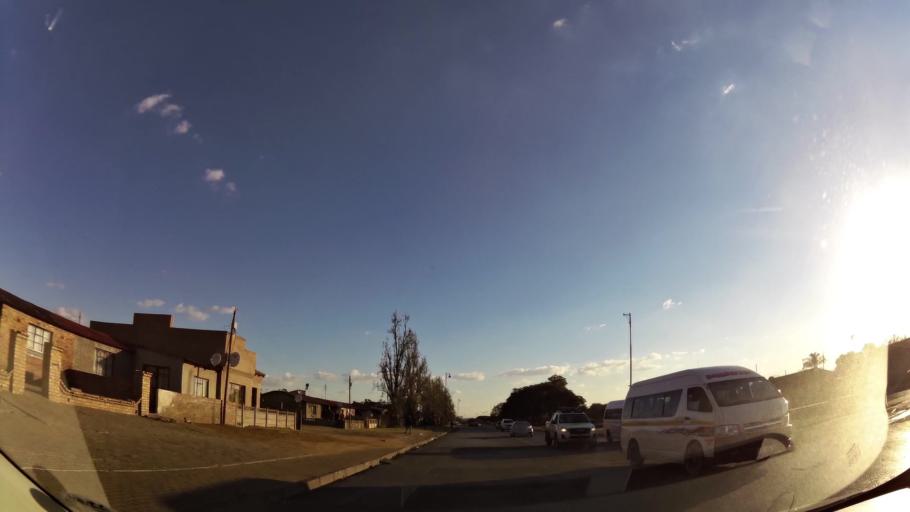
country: ZA
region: Mpumalanga
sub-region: Nkangala District Municipality
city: Witbank
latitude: -25.8804
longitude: 29.1919
